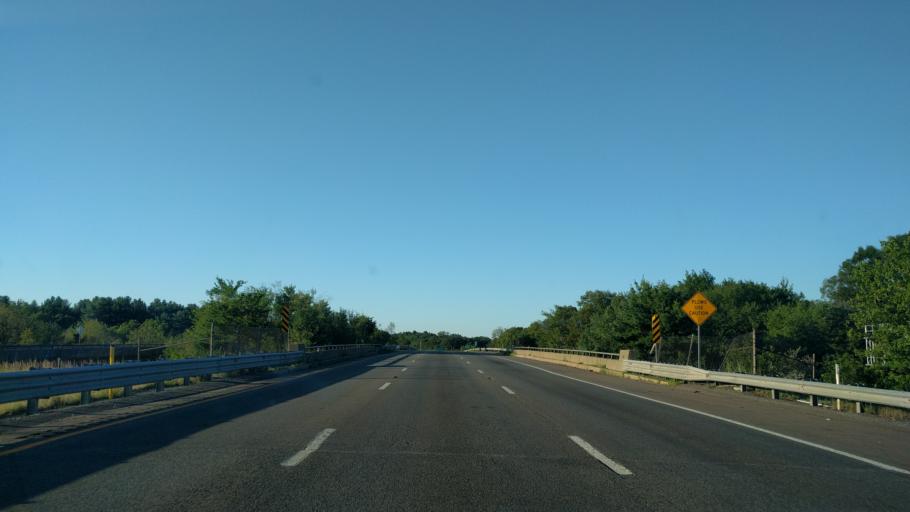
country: US
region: Massachusetts
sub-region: Worcester County
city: Cordaville
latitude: 42.2695
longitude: -71.5651
